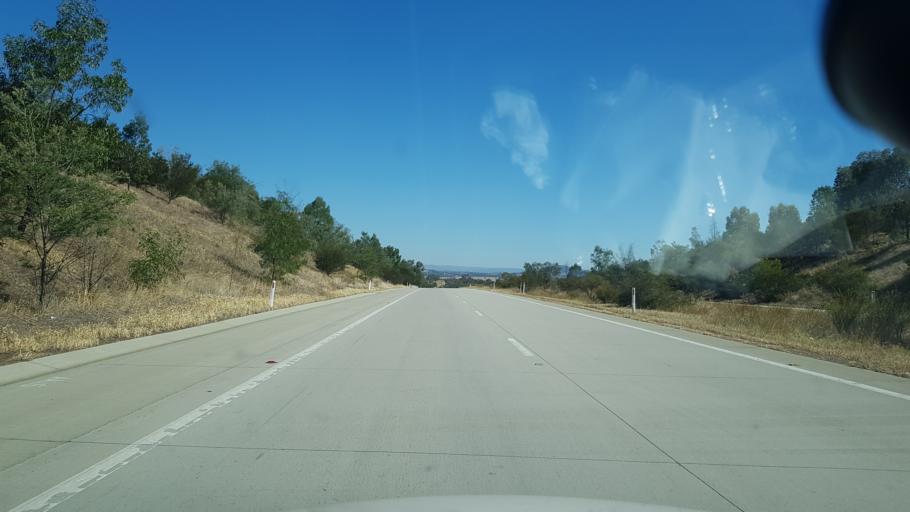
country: AU
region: New South Wales
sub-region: Albury Municipality
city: Lavington
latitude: -35.9193
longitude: 147.0963
